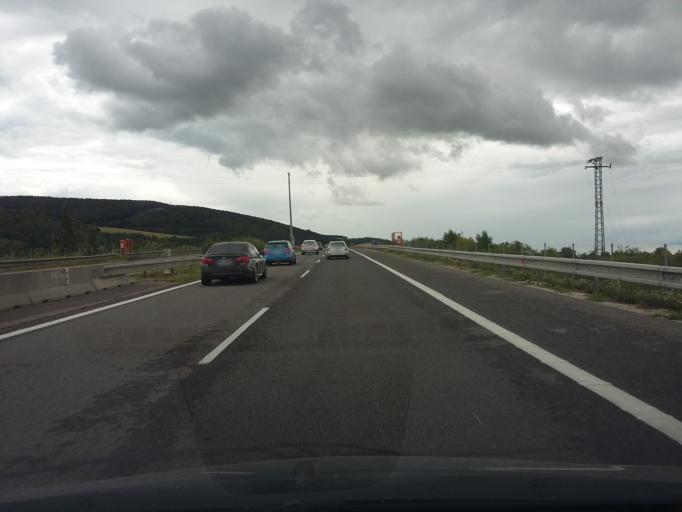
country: SK
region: Trenciansky
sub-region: Okres Nove Mesto nad Vahom
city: Nove Mesto nad Vahom
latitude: 48.8142
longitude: 17.9064
